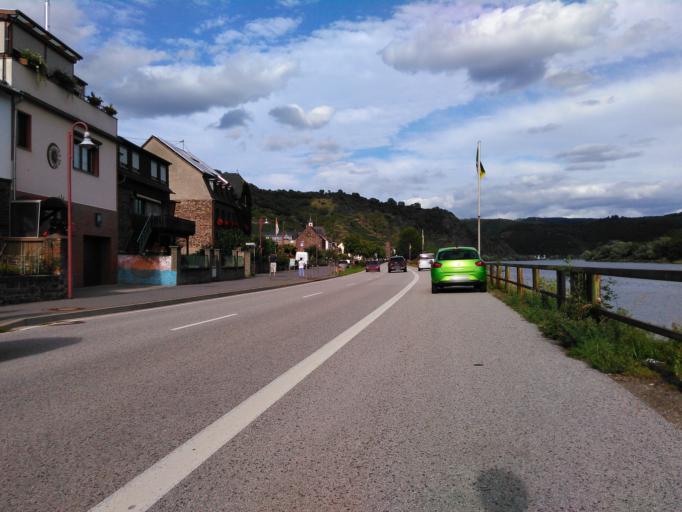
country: DE
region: Rheinland-Pfalz
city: Hatzenport
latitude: 50.2265
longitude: 7.4139
